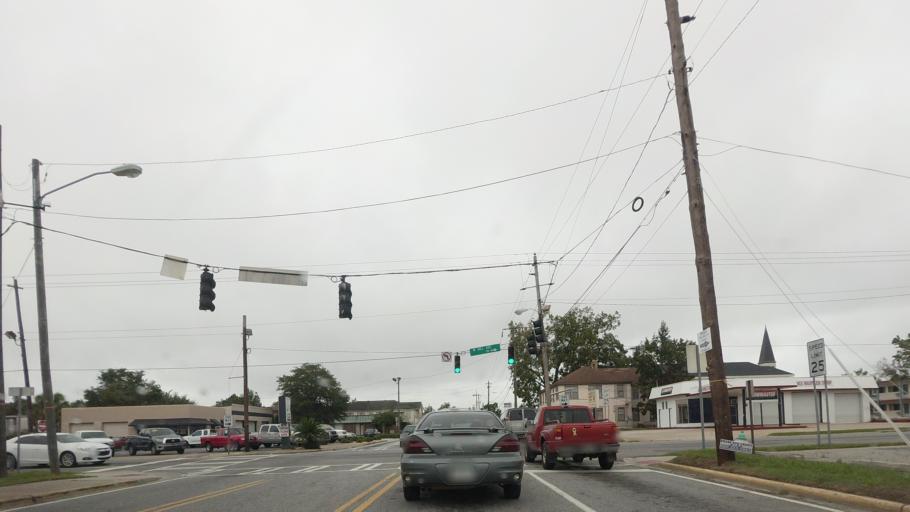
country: US
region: Georgia
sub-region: Lowndes County
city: Valdosta
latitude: 30.8295
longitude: -83.2816
